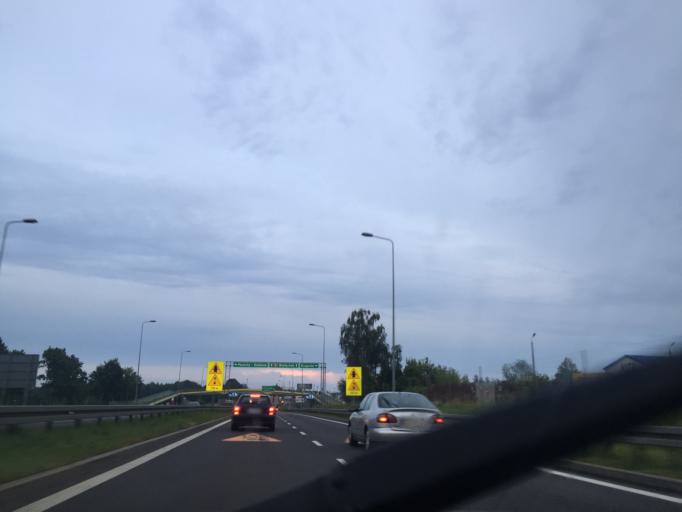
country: PL
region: Podlasie
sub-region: Powiat bialostocki
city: Choroszcz
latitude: 53.1502
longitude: 23.0497
